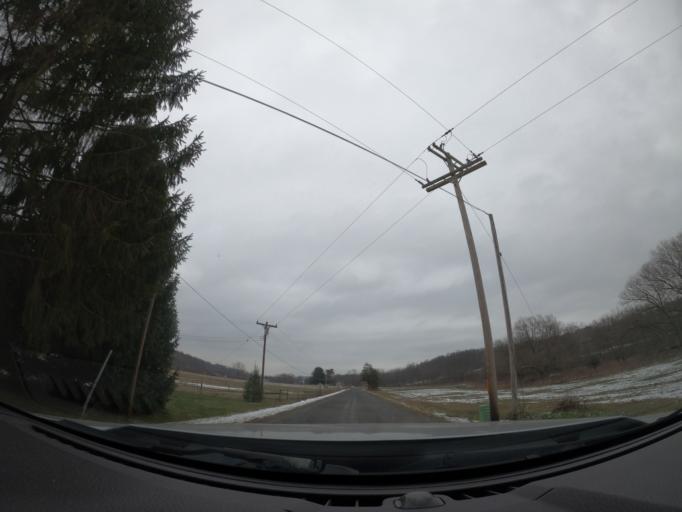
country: US
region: New York
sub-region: Cayuga County
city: Moravia
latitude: 42.6396
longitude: -76.4514
